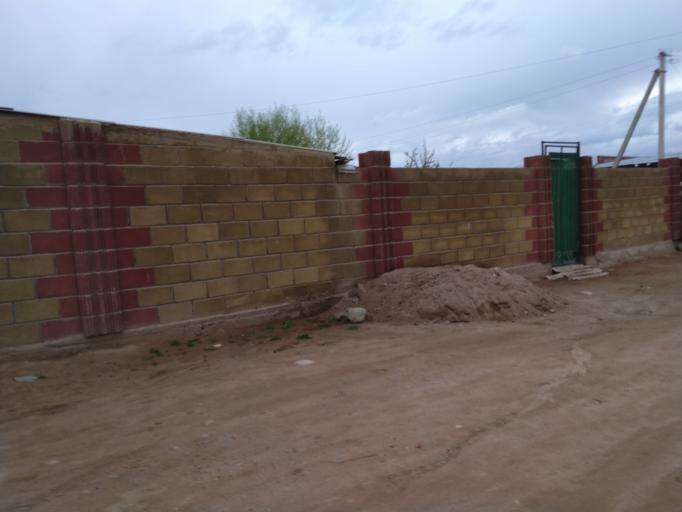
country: KG
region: Ysyk-Koel
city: Bokombayevskoye
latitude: 42.1127
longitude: 76.9833
